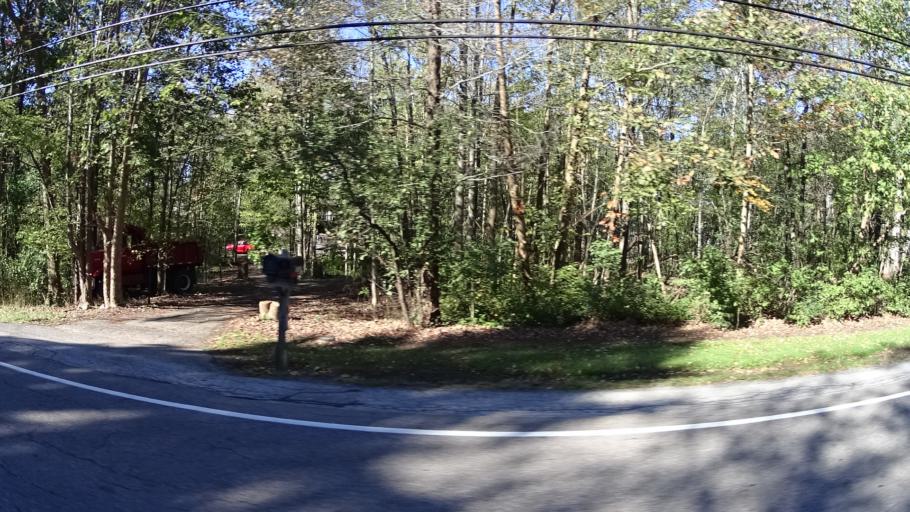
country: US
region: Ohio
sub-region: Lorain County
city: South Amherst
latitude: 41.3724
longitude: -82.2380
